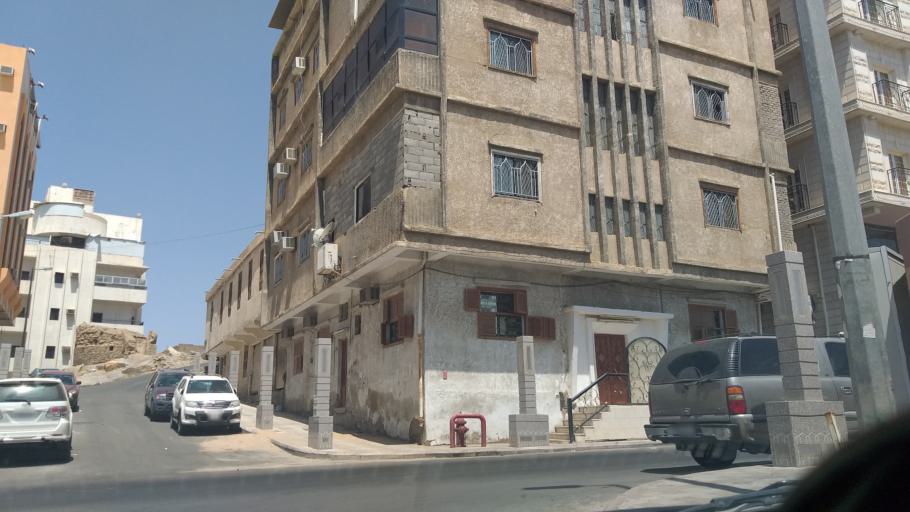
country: SA
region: Makkah
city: Ta'if
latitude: 21.2703
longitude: 40.4073
